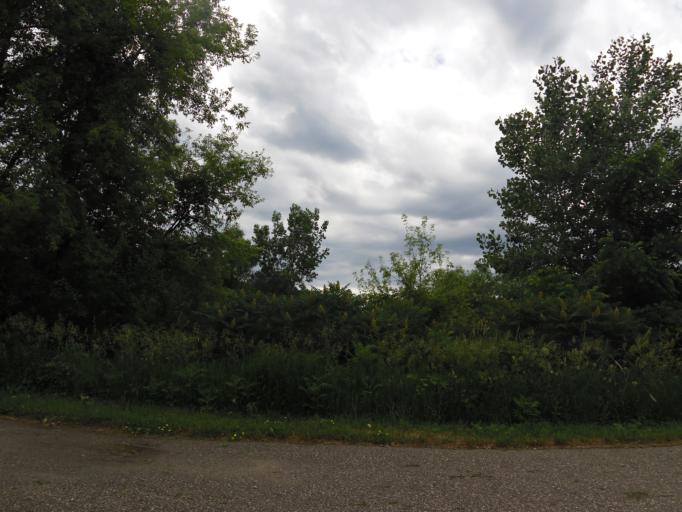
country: US
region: Minnesota
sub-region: Scott County
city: Prior Lake
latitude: 44.7099
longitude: -93.4356
